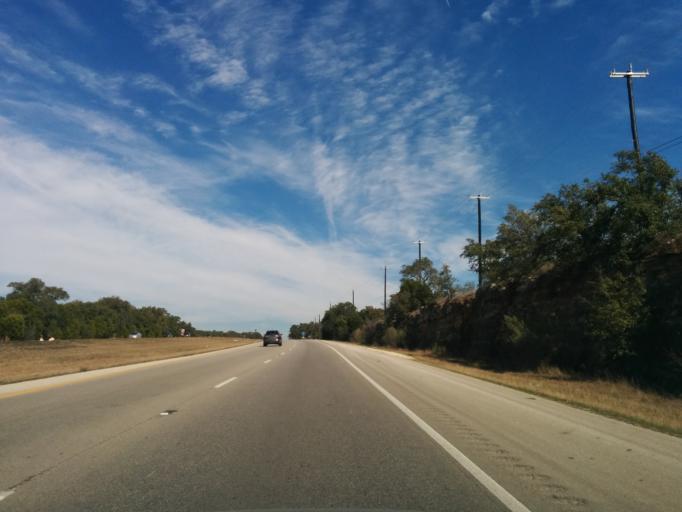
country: US
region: Texas
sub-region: Comal County
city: Bulverde
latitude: 29.7571
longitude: -98.4303
